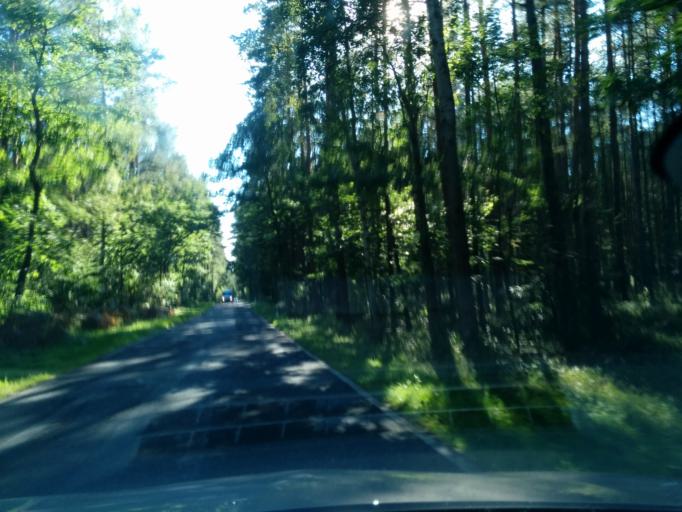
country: DE
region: Mecklenburg-Vorpommern
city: Torgelow
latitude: 53.6723
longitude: 14.0283
